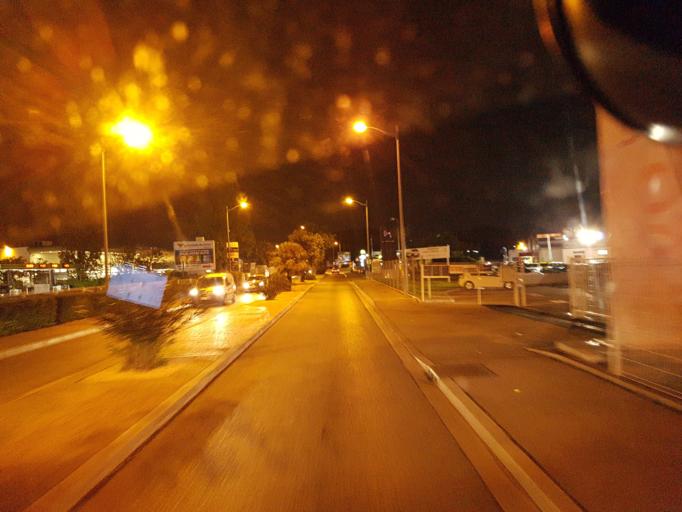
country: FR
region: Provence-Alpes-Cote d'Azur
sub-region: Departement des Bouches-du-Rhone
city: Saint-Victoret
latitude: 43.4170
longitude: 5.2274
